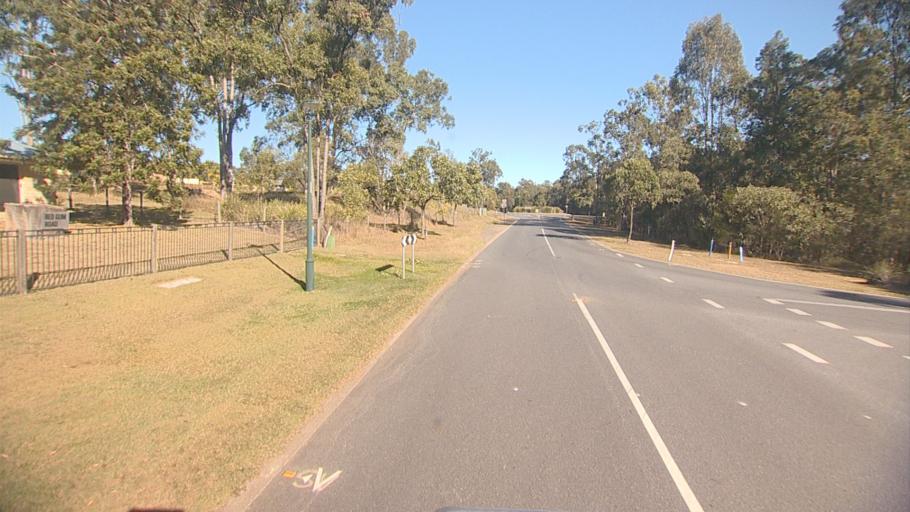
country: AU
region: Queensland
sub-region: Logan
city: North Maclean
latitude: -27.7524
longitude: 152.9574
